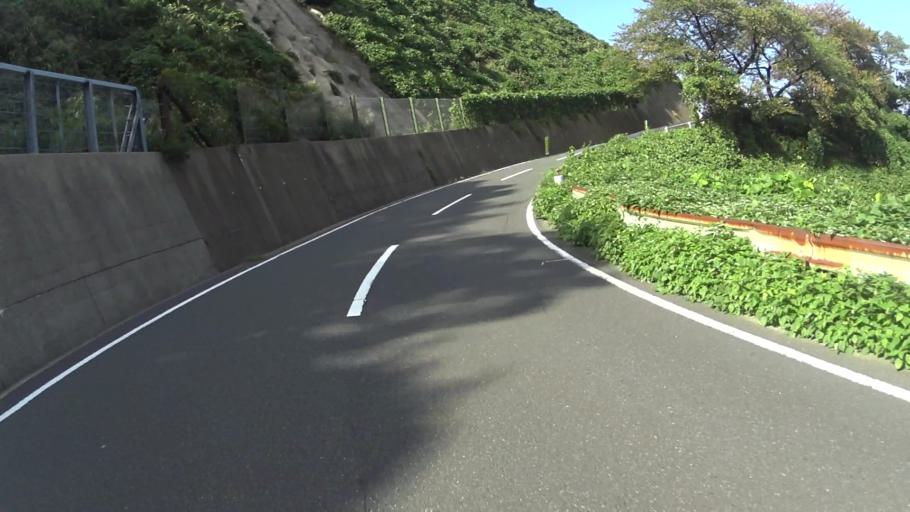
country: JP
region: Kyoto
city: Miyazu
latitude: 35.7647
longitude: 135.2343
